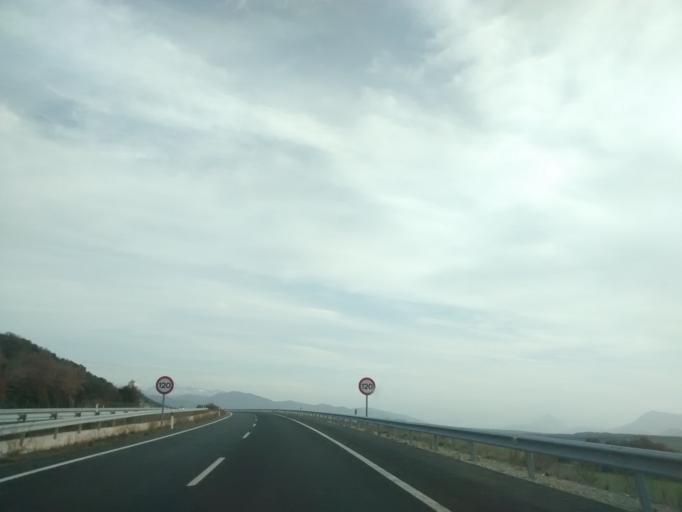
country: ES
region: Aragon
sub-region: Provincia de Zaragoza
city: Artieda
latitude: 42.6084
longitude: -0.9732
